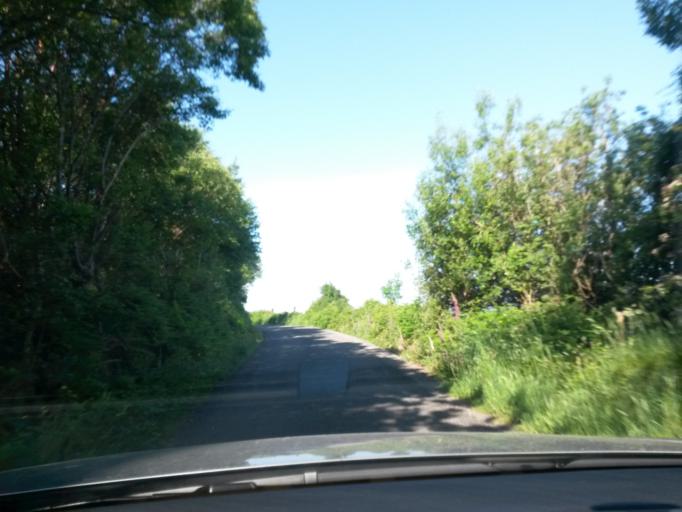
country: IE
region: Munster
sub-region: Ciarrai
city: Kenmare
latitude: 51.7942
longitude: -9.7996
